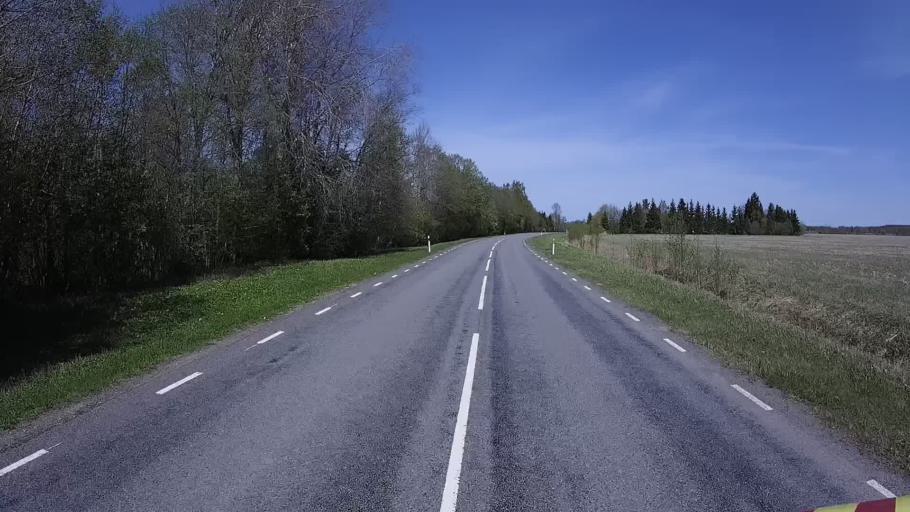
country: EE
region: Laeaene
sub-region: Lihula vald
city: Lihula
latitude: 58.6521
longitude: 23.8387
